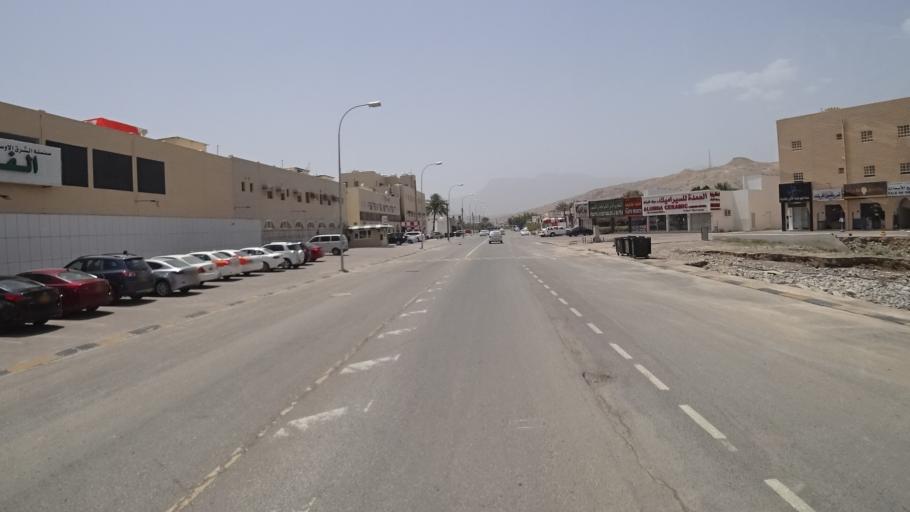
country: OM
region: Muhafazat Masqat
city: Muscat
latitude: 23.2418
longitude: 58.9029
